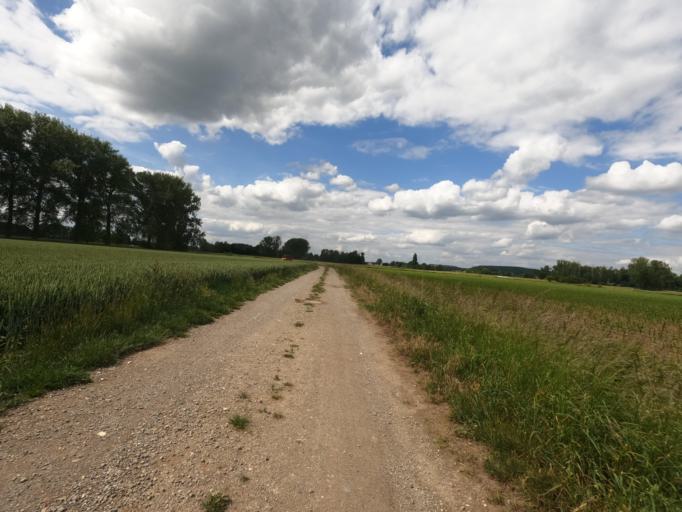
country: DE
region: North Rhine-Westphalia
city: Huckelhoven
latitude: 51.0289
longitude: 6.2029
